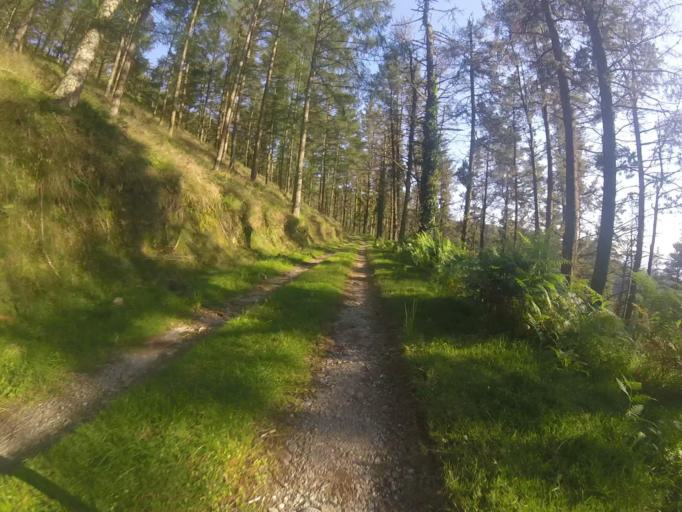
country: ES
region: Navarre
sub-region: Provincia de Navarra
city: Arano
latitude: 43.2468
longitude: -1.8520
